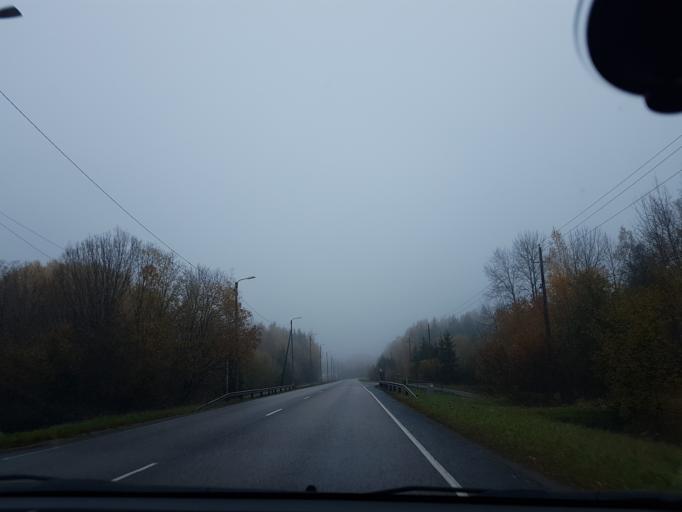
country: FI
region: Uusimaa
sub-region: Helsinki
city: Tuusula
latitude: 60.4242
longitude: 25.0537
